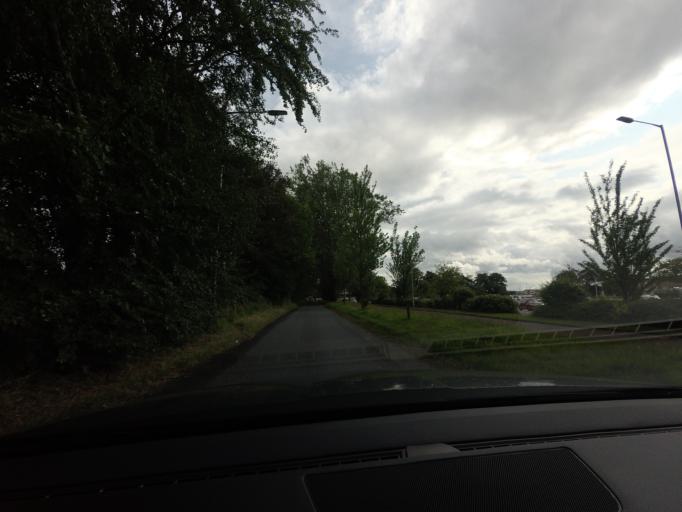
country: GB
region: Scotland
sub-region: Highland
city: Inverness
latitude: 57.4702
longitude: -4.1876
